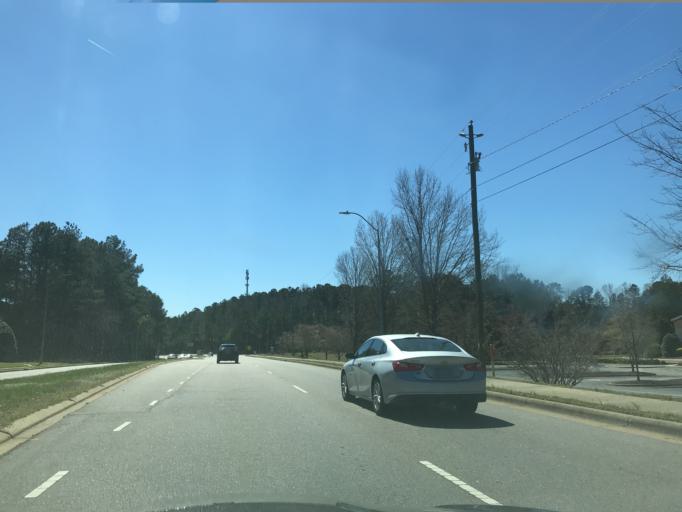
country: US
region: North Carolina
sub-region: Wake County
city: Garner
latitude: 35.6911
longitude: -78.6347
